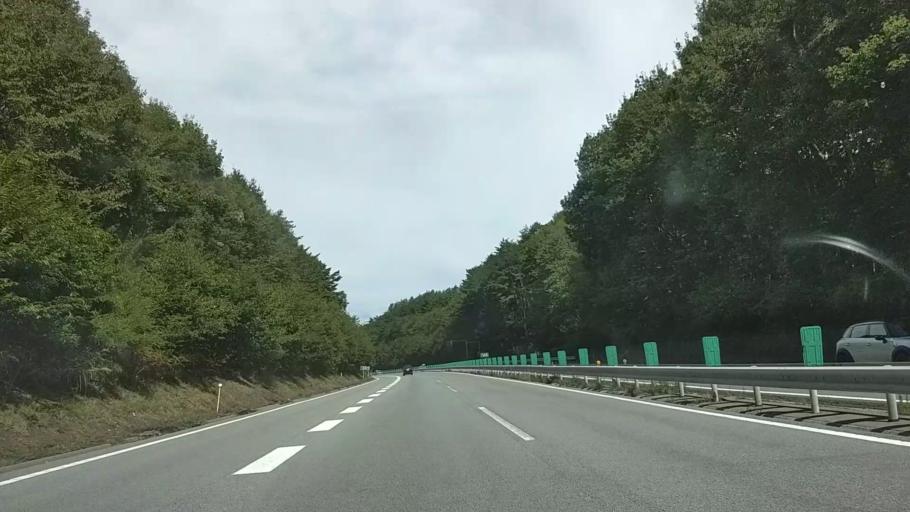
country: JP
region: Yamanashi
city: Nirasaki
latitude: 35.8577
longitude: 138.3324
